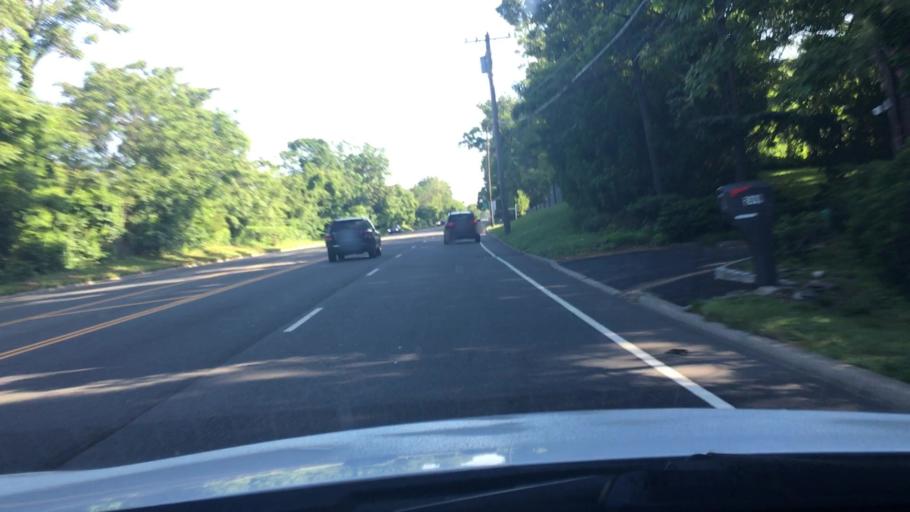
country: US
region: New York
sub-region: Nassau County
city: East Williston
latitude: 40.7736
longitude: -73.6249
